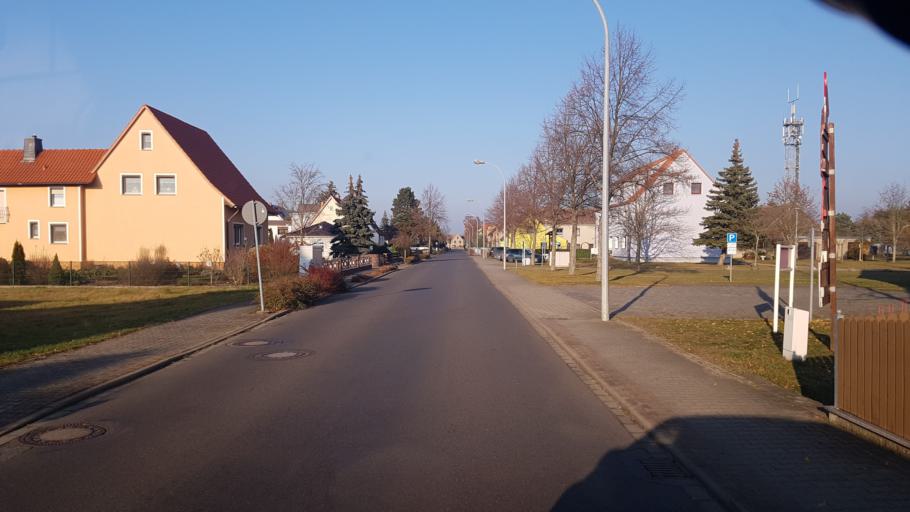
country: DE
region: Brandenburg
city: Tettau
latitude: 51.4274
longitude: 13.7282
